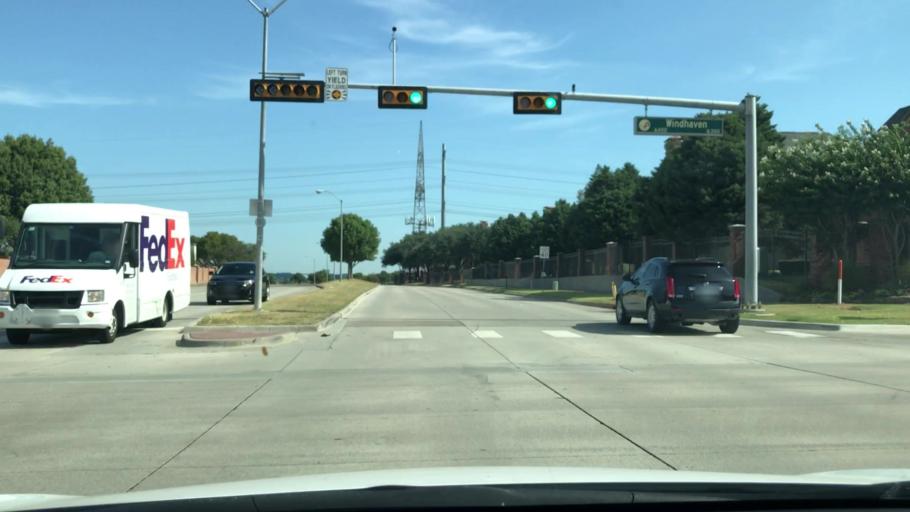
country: US
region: Texas
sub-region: Denton County
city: The Colony
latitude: 33.0569
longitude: -96.8384
